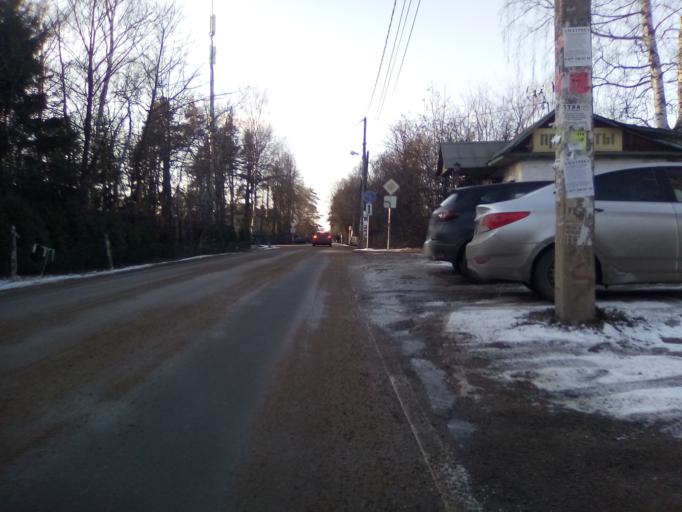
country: RU
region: Moskovskaya
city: Lesnoy Gorodok
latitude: 55.6650
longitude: 37.2128
